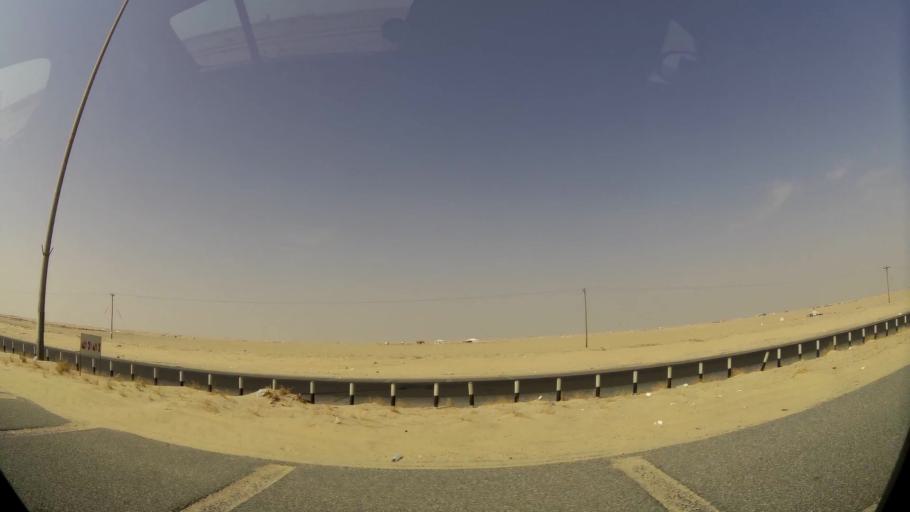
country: KW
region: Al Ahmadi
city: Al Wafrah
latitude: 28.8217
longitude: 48.0488
